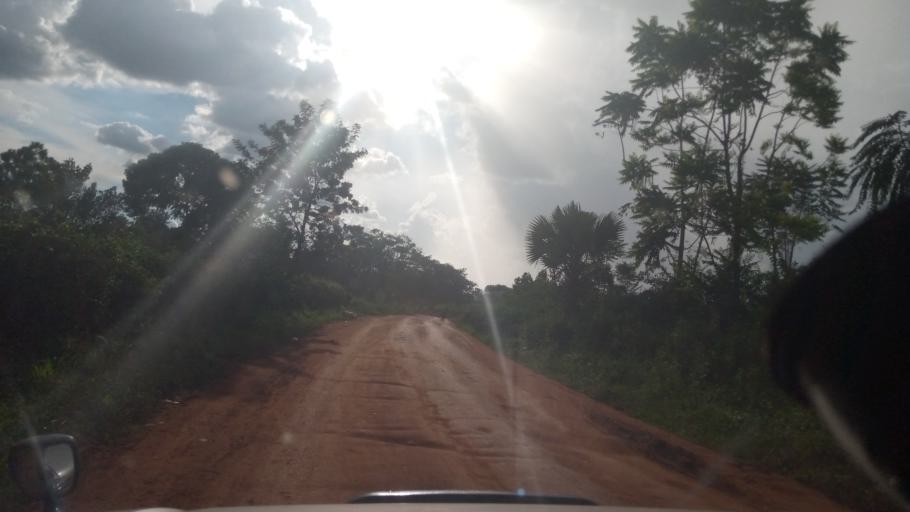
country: UG
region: Northern Region
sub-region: Lira District
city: Lira
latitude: 2.2283
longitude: 32.9018
